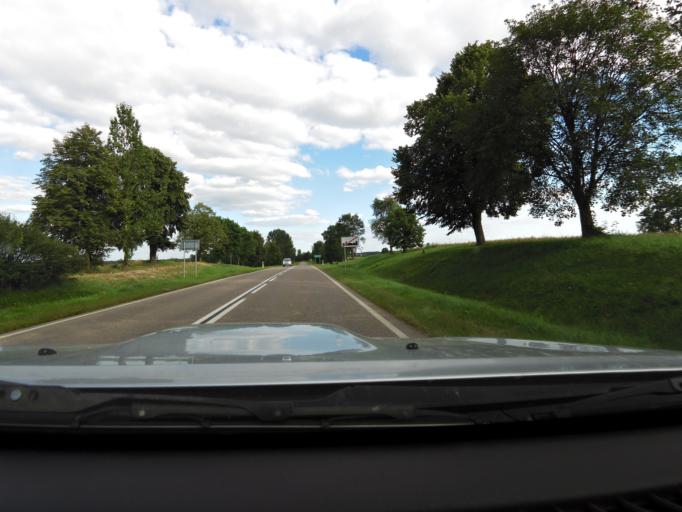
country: PL
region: Podlasie
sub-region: Powiat suwalski
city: Raczki
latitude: 53.8482
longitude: 22.7870
